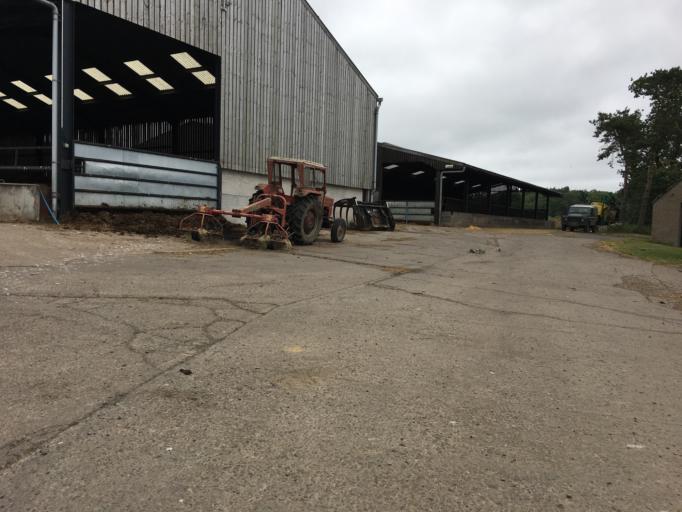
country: GB
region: England
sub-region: Northumberland
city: Belford
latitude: 55.6086
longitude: -1.8678
